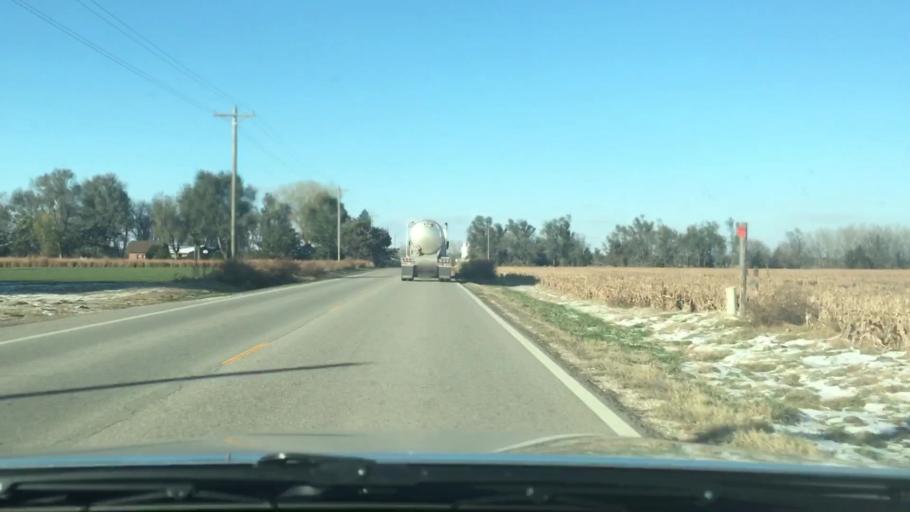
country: US
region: Kansas
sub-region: Rice County
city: Sterling
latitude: 38.1897
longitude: -98.2068
